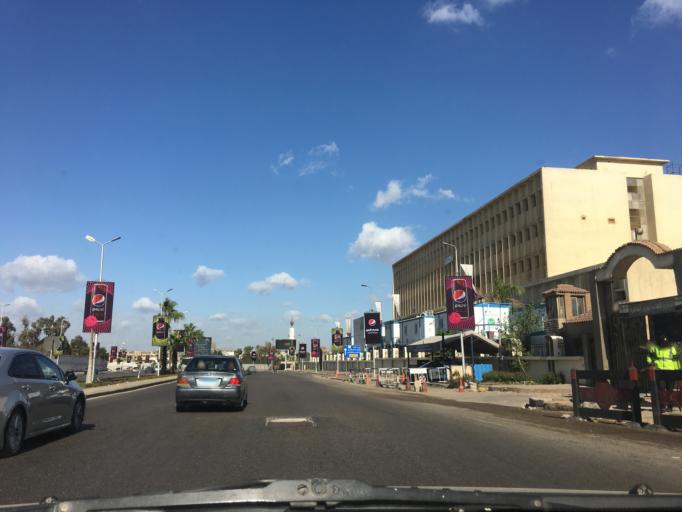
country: EG
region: Muhafazat al Qahirah
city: Cairo
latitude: 30.0535
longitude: 31.3074
